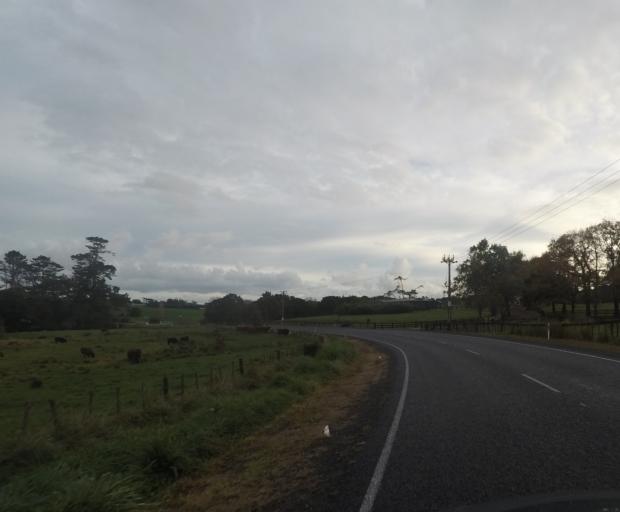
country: NZ
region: Auckland
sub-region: Auckland
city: Wellsford
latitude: -36.2149
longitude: 174.5870
